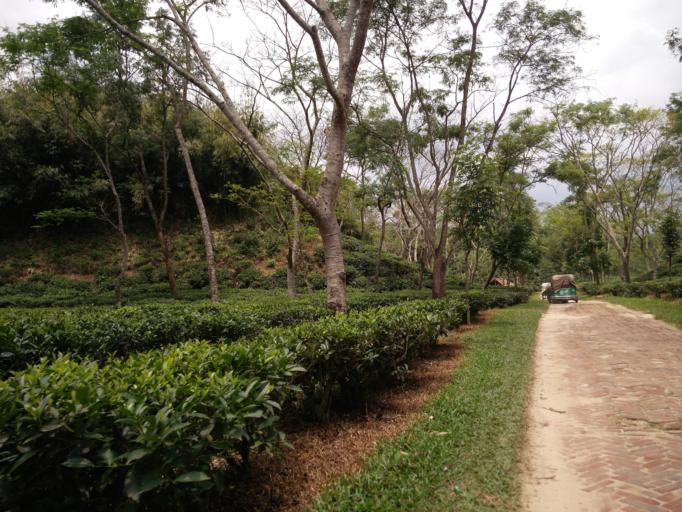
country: IN
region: Tripura
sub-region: Dhalai
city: Kamalpur
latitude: 24.3051
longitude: 91.8009
